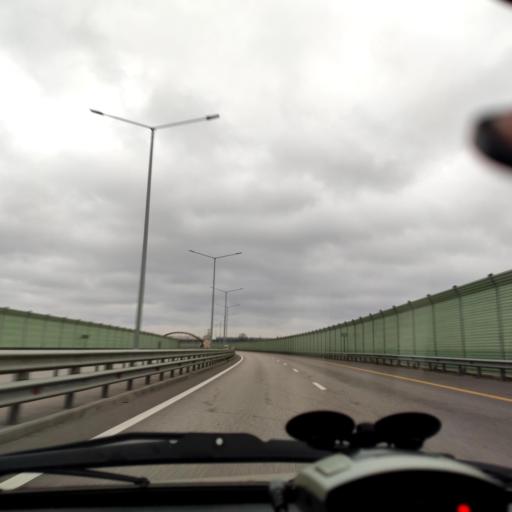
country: RU
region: Voronezj
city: Novaya Usman'
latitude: 51.6092
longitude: 39.3221
